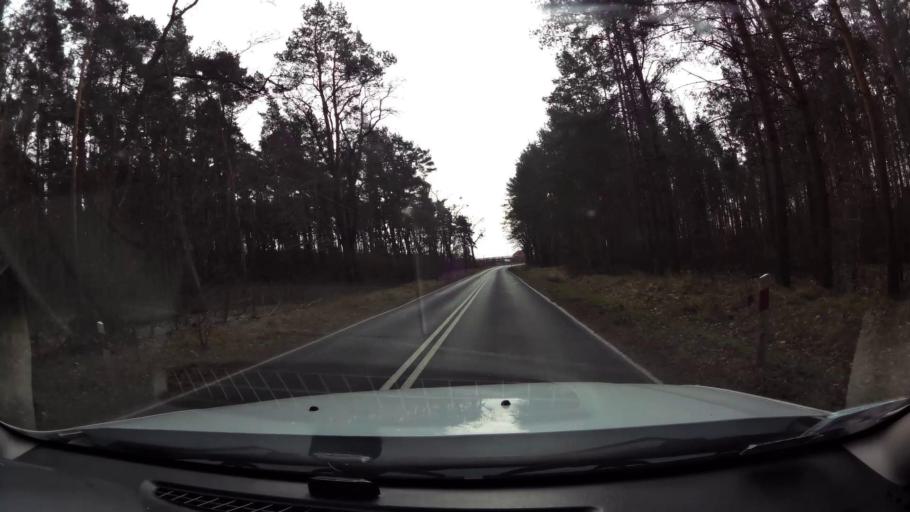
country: PL
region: West Pomeranian Voivodeship
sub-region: Powiat mysliborski
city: Debno
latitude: 52.7561
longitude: 14.6866
